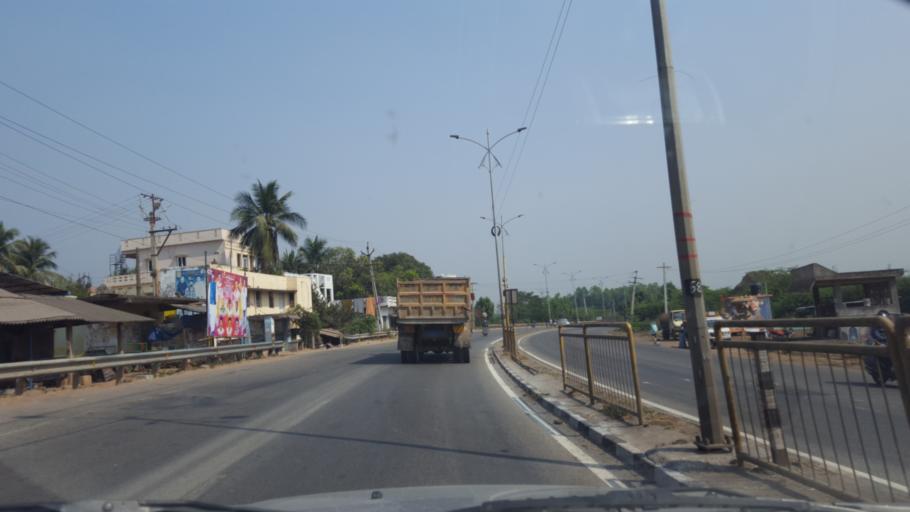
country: IN
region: Andhra Pradesh
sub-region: Vishakhapatnam
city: Anakapalle
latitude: 17.6894
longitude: 83.0742
